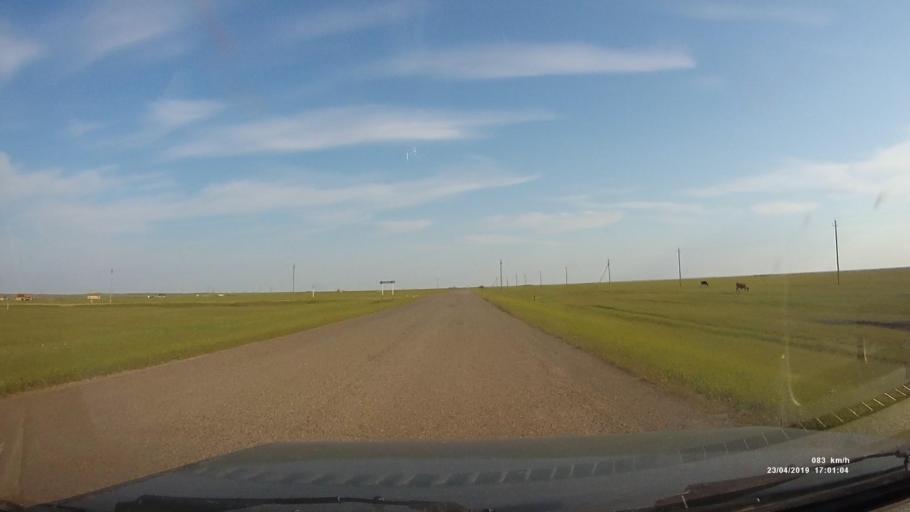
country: RU
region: Kalmykiya
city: Priyutnoye
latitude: 46.3000
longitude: 43.4069
